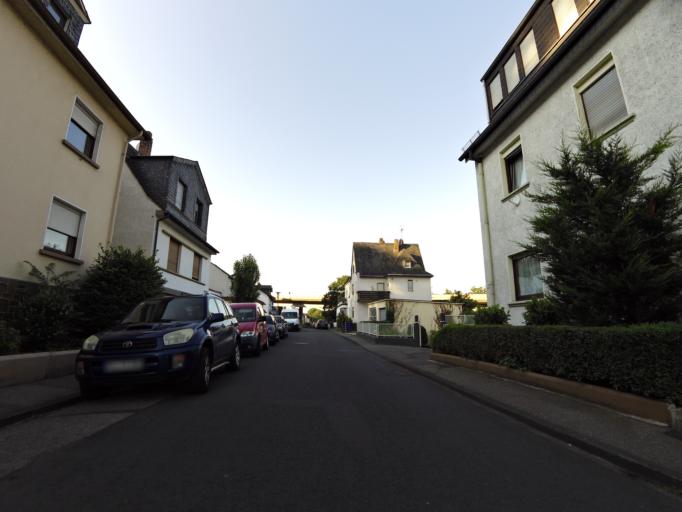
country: DE
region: Rheinland-Pfalz
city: Koblenz
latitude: 50.3317
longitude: 7.5995
